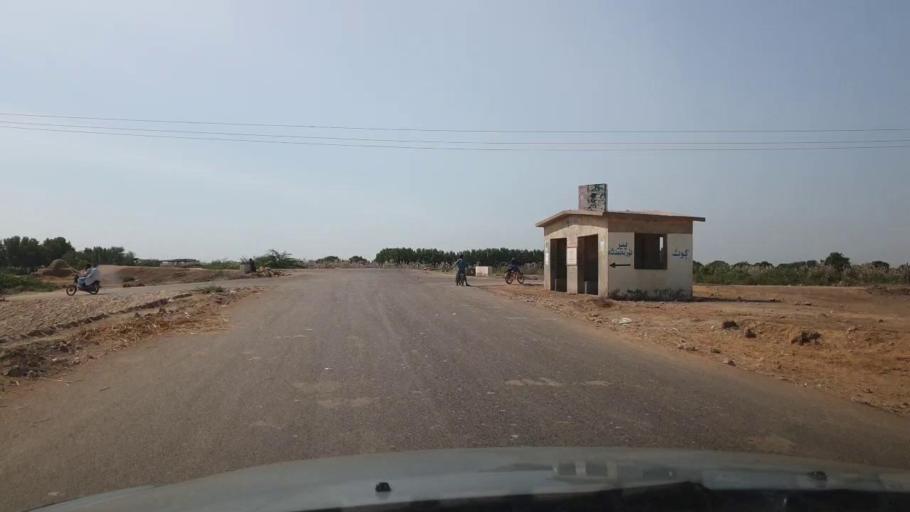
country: PK
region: Sindh
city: Tando Muhammad Khan
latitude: 25.1570
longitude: 68.3790
